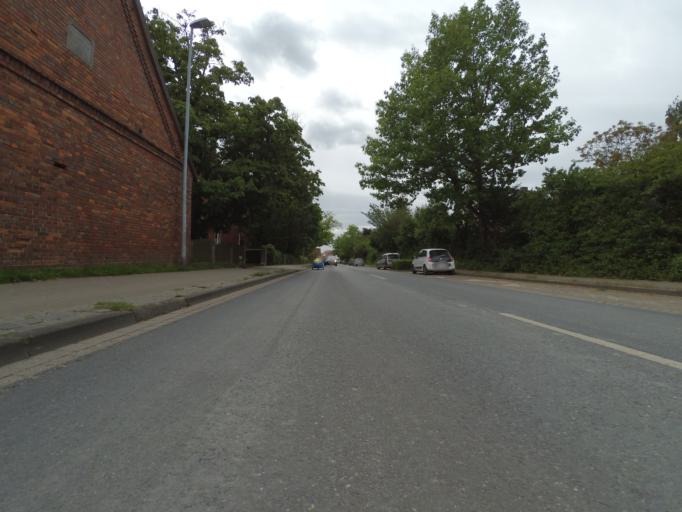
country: DE
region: Lower Saxony
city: Isernhagen Farster Bauerschaft
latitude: 52.4570
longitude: 9.8050
